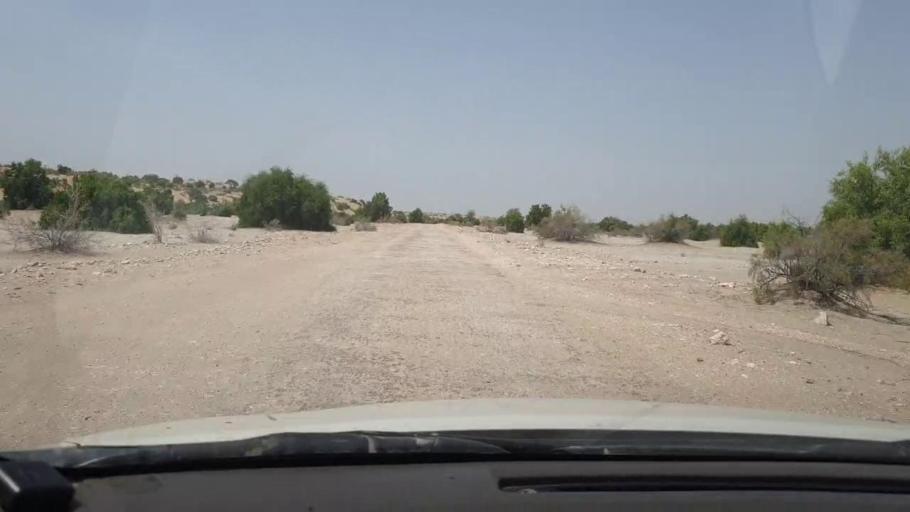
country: PK
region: Sindh
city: Rohri
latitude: 27.2961
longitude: 69.2718
